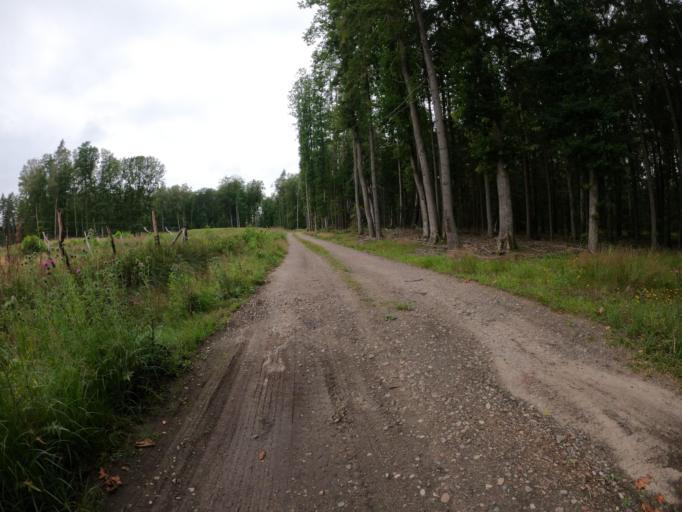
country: PL
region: West Pomeranian Voivodeship
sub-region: Powiat szczecinecki
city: Grzmiaca
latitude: 53.9766
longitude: 16.4211
